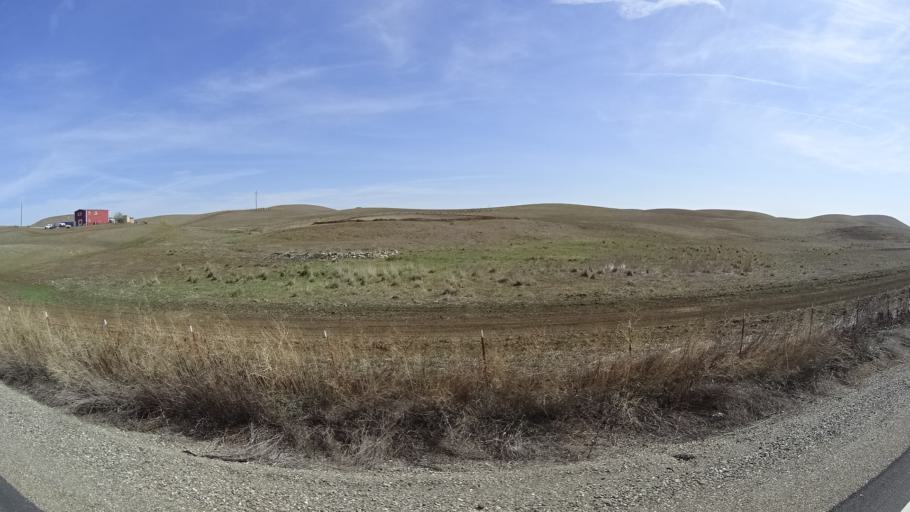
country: US
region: California
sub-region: Glenn County
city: Willows
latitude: 39.5508
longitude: -122.3564
